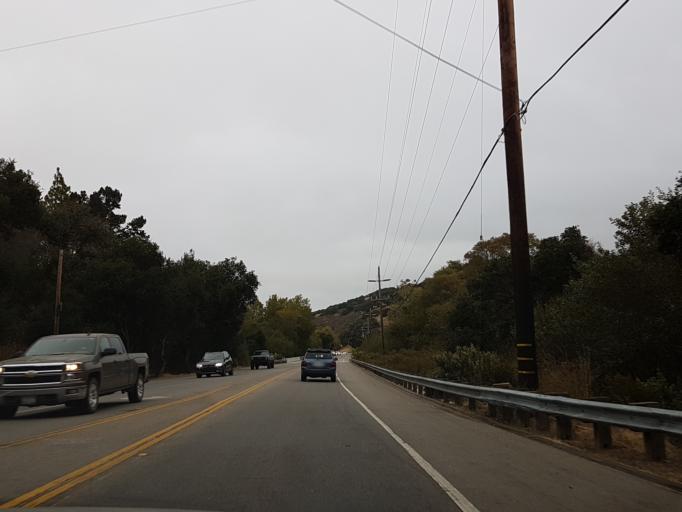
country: US
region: California
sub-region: Monterey County
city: Carmel Valley Village
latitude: 36.5804
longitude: -121.7196
